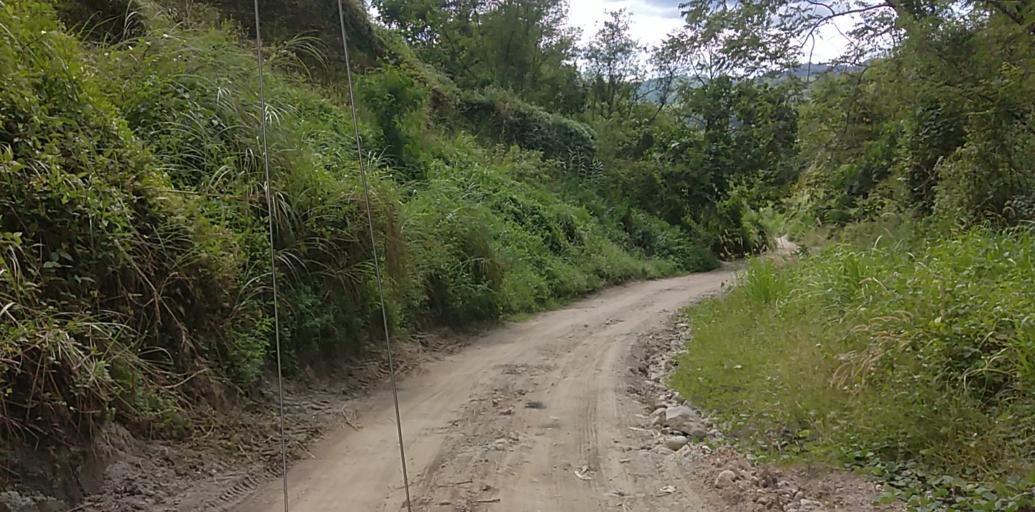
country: PH
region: Central Luzon
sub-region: Province of Pampanga
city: Dolores
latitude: 15.1138
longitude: 120.5045
